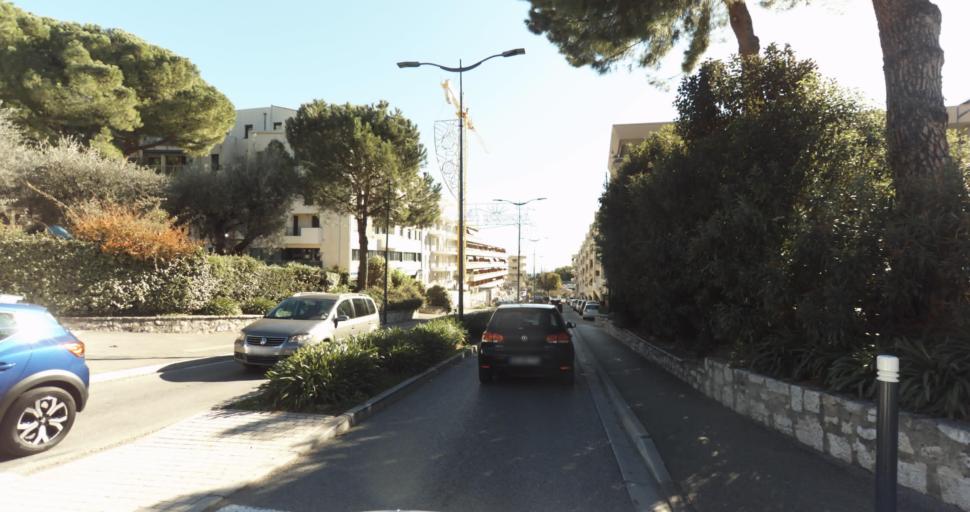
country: FR
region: Provence-Alpes-Cote d'Azur
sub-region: Departement des Alpes-Maritimes
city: Vence
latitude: 43.7228
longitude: 7.1076
